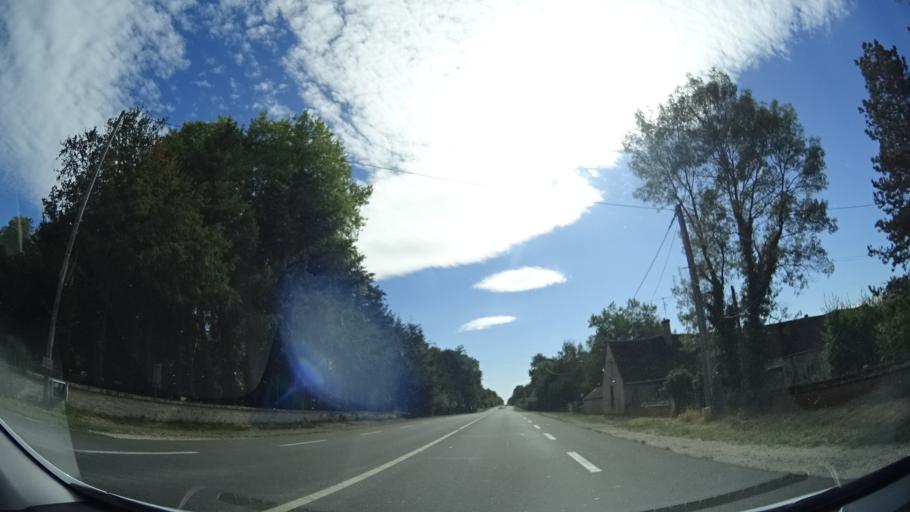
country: FR
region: Centre
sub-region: Departement du Loiret
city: Vitry-aux-Loges
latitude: 47.9376
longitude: 2.3515
